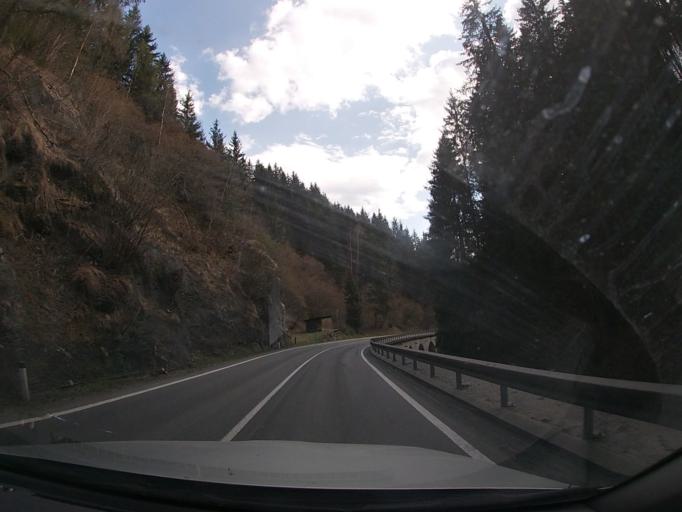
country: AT
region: Styria
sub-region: Politischer Bezirk Murau
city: Neumarkt in Steiermark
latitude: 47.0848
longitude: 14.4294
